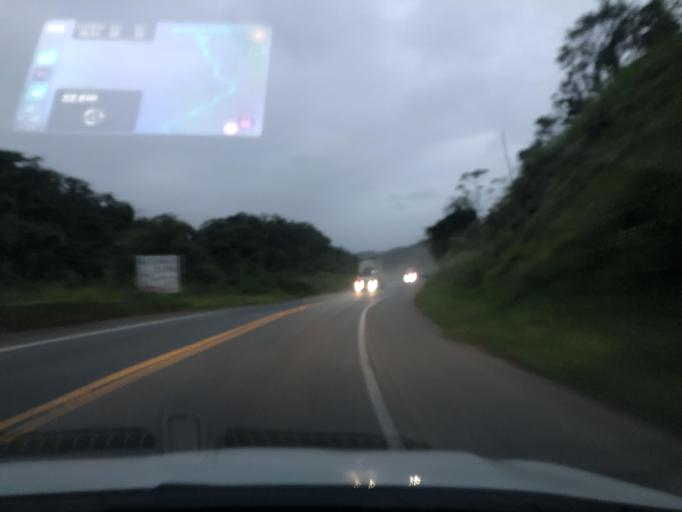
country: BR
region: Santa Catarina
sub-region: Jaragua Do Sul
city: Jaragua do Sul
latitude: -26.6538
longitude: -49.0264
